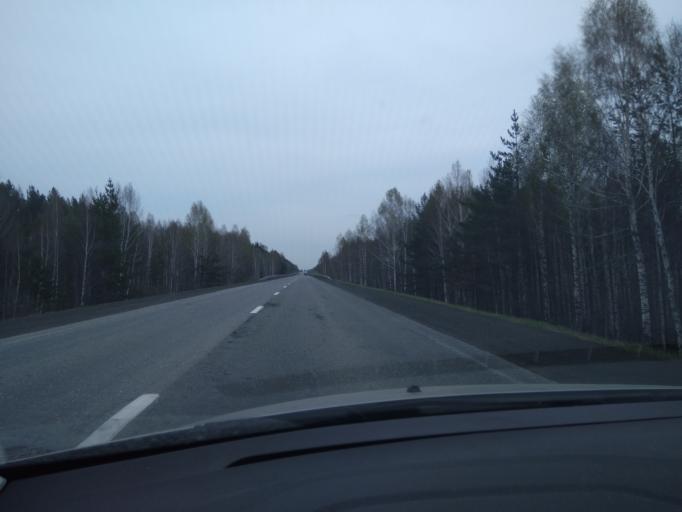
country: RU
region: Sverdlovsk
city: Beloyarskiy
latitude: 56.7760
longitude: 61.5420
